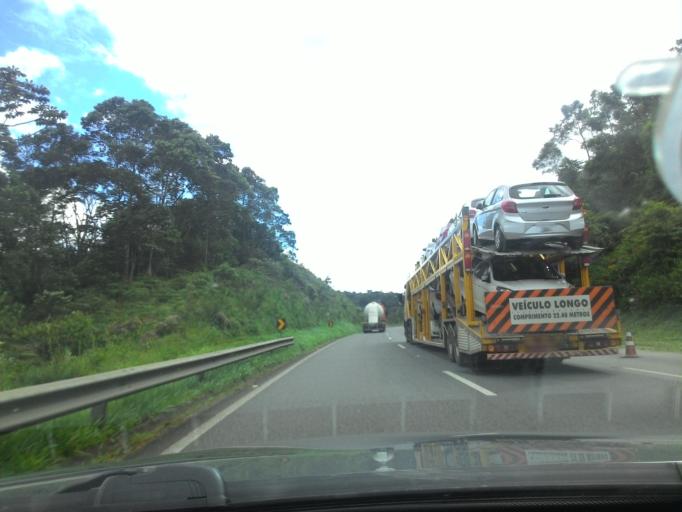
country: BR
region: Sao Paulo
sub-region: Cajati
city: Cajati
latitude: -24.9015
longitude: -48.2486
